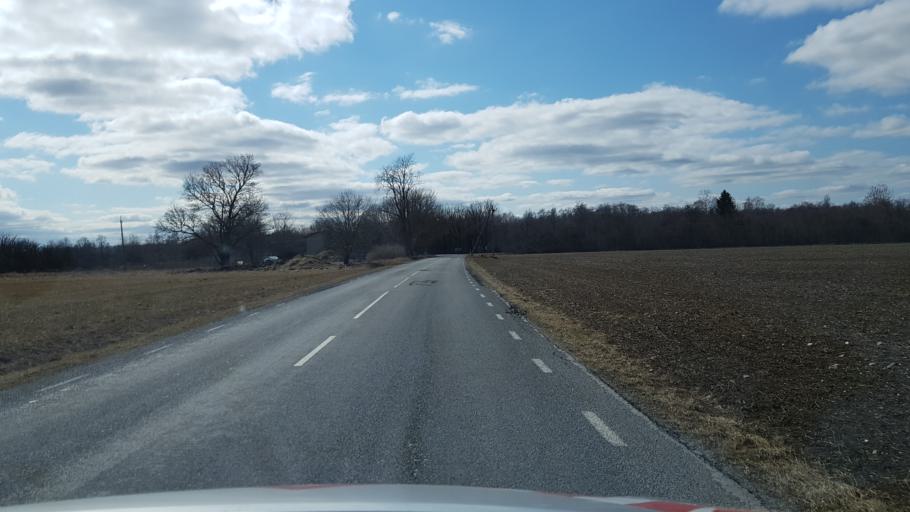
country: EE
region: Laeaene-Virumaa
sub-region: Tapa vald
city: Tapa
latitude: 59.2669
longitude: 25.8525
